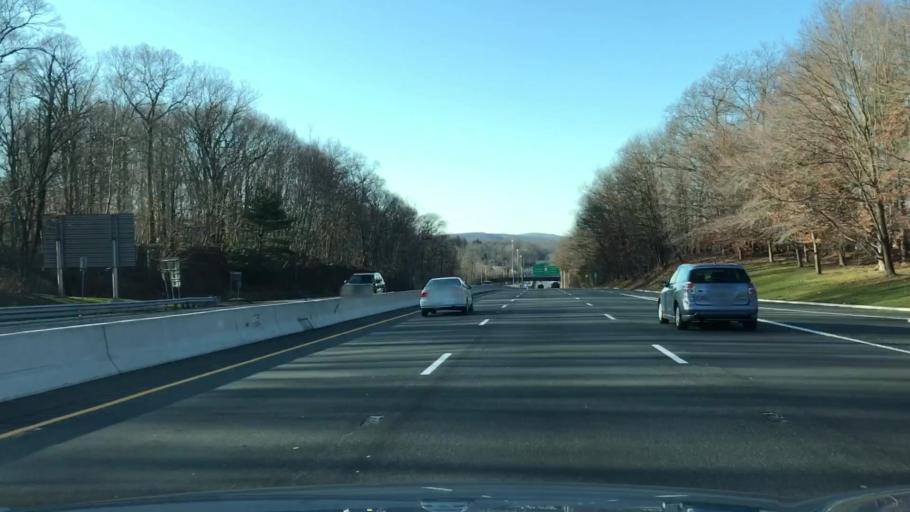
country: US
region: New Jersey
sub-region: Bergen County
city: Franklin Lakes
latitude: 41.0142
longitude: -74.2088
